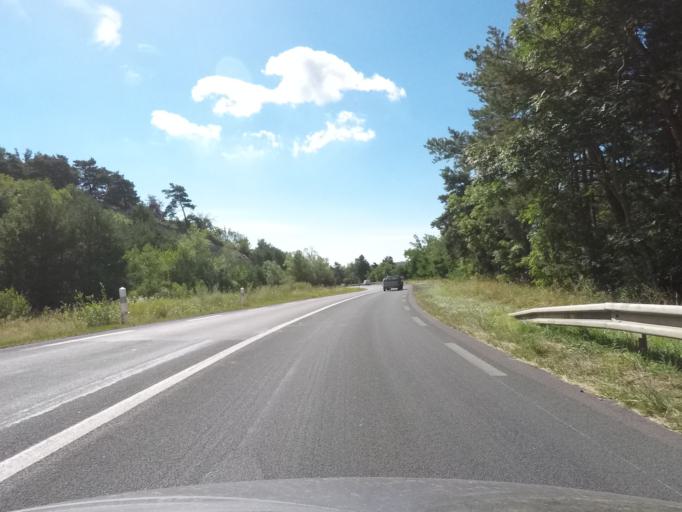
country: FR
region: Auvergne
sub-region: Departement du Puy-de-Dome
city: Ceyrat
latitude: 45.7089
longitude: 3.0589
